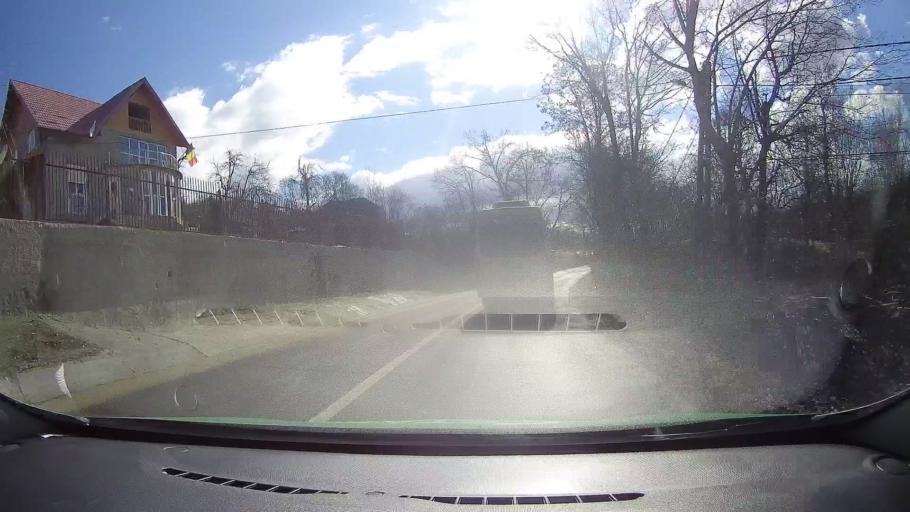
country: RO
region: Dambovita
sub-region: Comuna Runcu
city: Badeni
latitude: 45.1446
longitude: 25.4043
